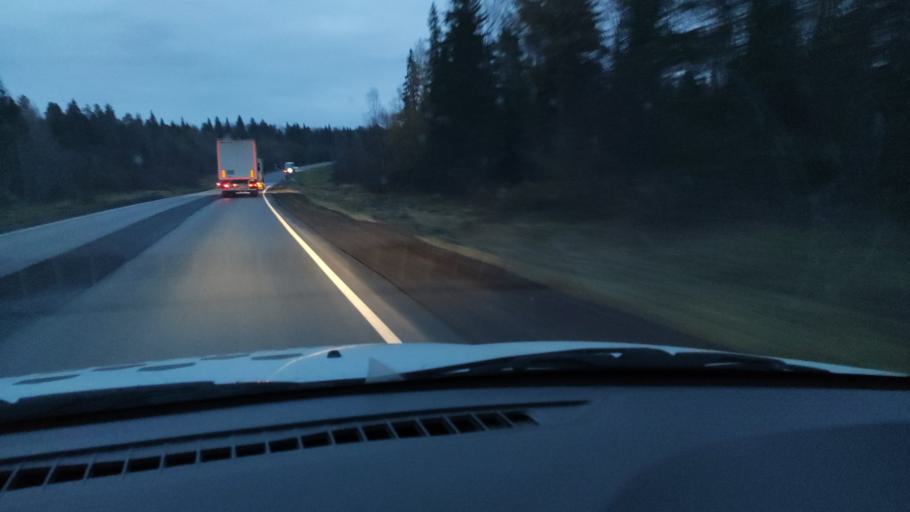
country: RU
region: Kirov
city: Kostino
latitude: 58.8304
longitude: 53.4000
